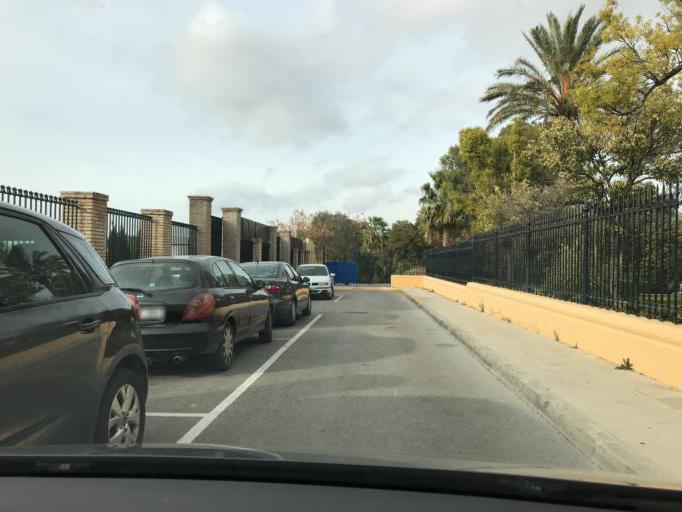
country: ES
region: Andalusia
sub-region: Provincia de Sevilla
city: Osuna
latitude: 37.2411
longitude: -5.1094
